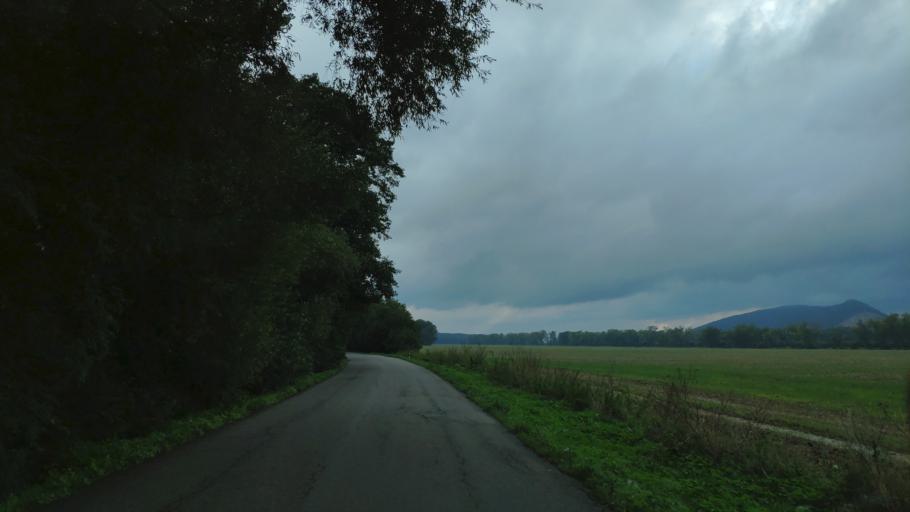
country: SK
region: Kosicky
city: Moldava nad Bodvou
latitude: 48.5875
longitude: 20.8966
